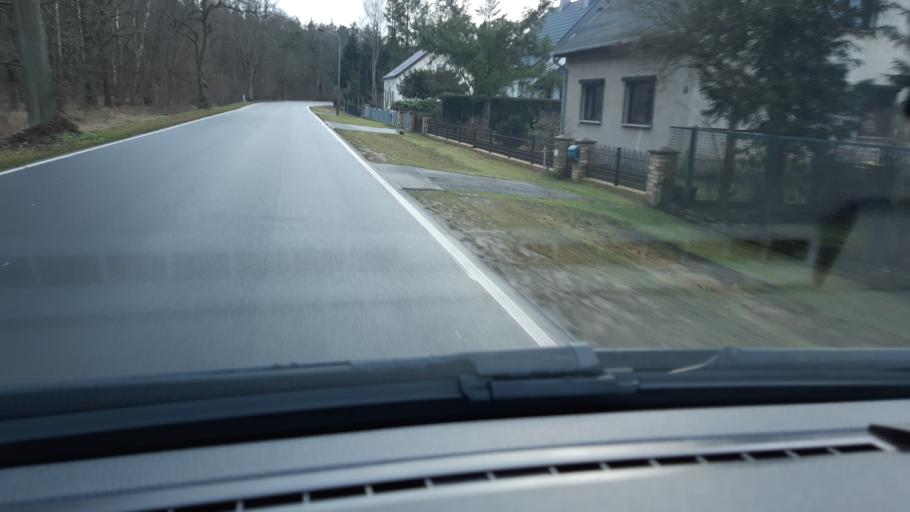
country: DE
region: Brandenburg
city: Zehdenick
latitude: 53.0321
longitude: 13.3858
